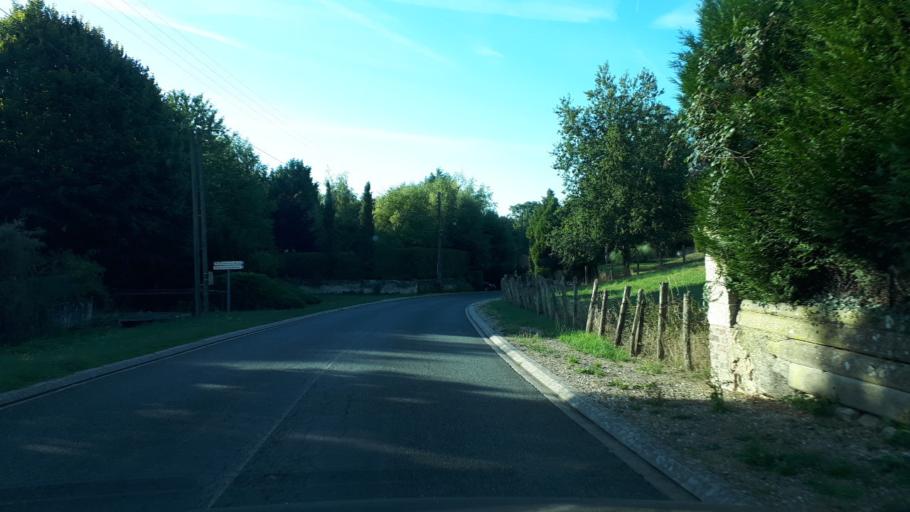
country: FR
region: Centre
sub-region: Departement du Loir-et-Cher
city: Lunay
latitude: 47.7541
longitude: 0.9386
